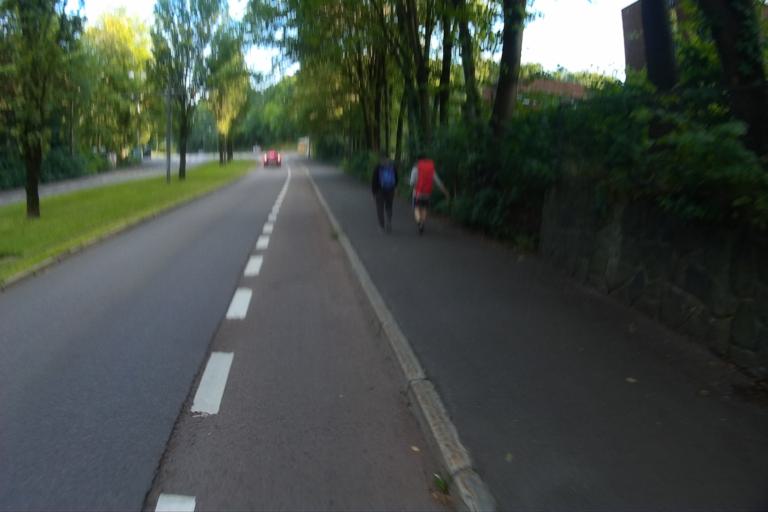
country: NO
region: Oslo
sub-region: Oslo
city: Oslo
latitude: 59.9386
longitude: 10.7299
